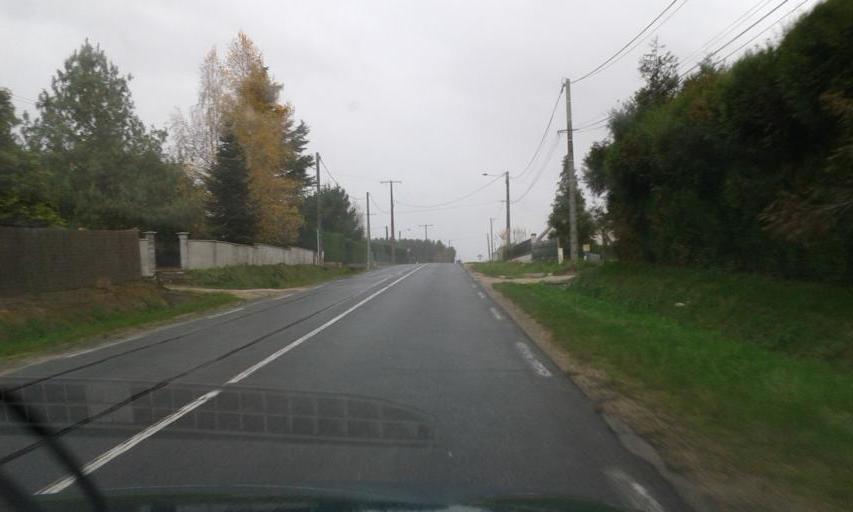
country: FR
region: Centre
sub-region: Departement du Loiret
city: Fay-aux-Loges
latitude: 47.9184
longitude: 2.1355
